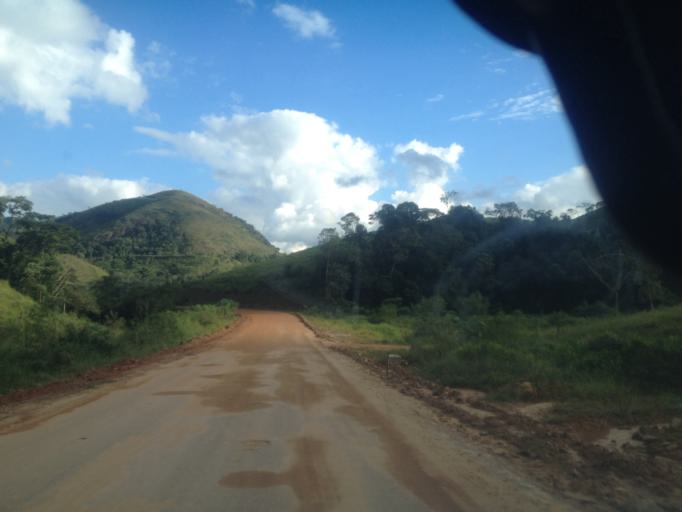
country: BR
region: Rio de Janeiro
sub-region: Quatis
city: Quatis
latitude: -22.2241
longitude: -44.2522
